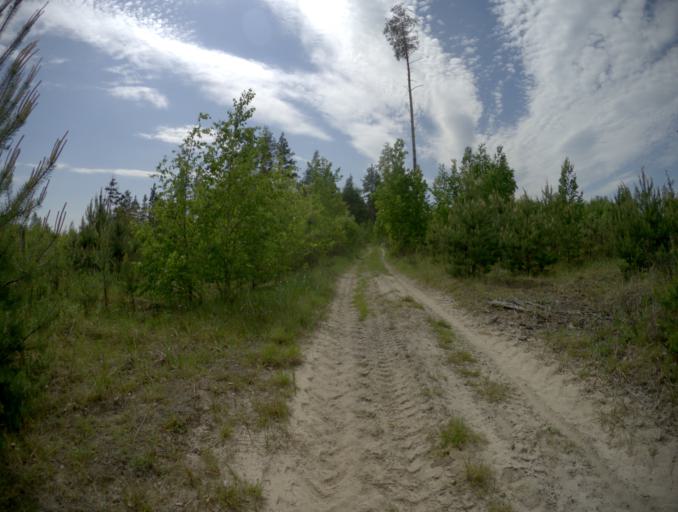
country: RU
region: Vladimir
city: Ivanishchi
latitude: 55.7049
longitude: 40.4666
